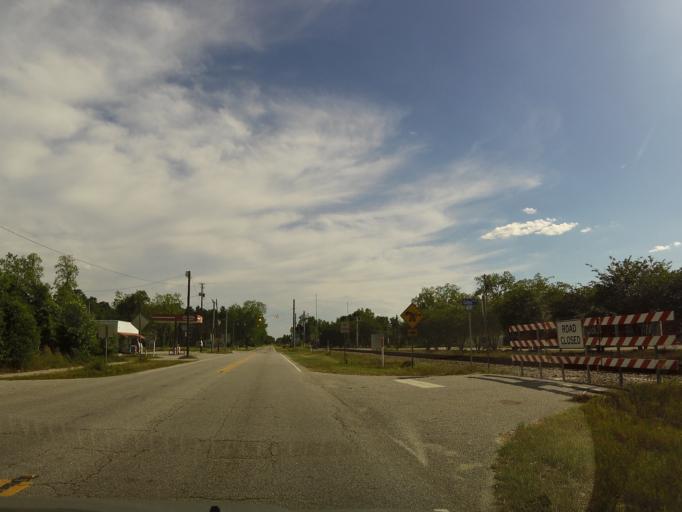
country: US
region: South Carolina
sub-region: Allendale County
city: Fairfax
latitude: 33.0372
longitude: -81.2219
